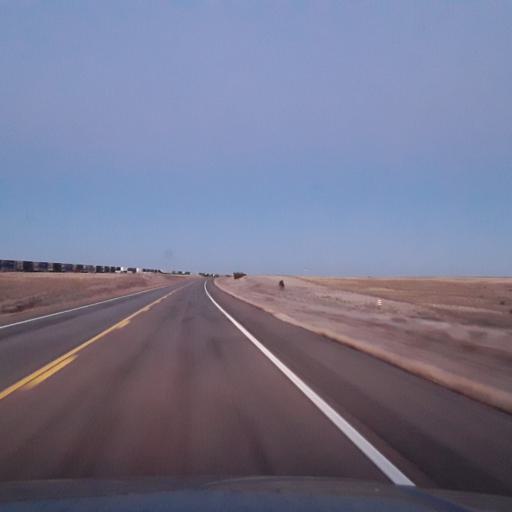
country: US
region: New Mexico
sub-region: Guadalupe County
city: Santa Rosa
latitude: 34.7477
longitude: -105.0147
